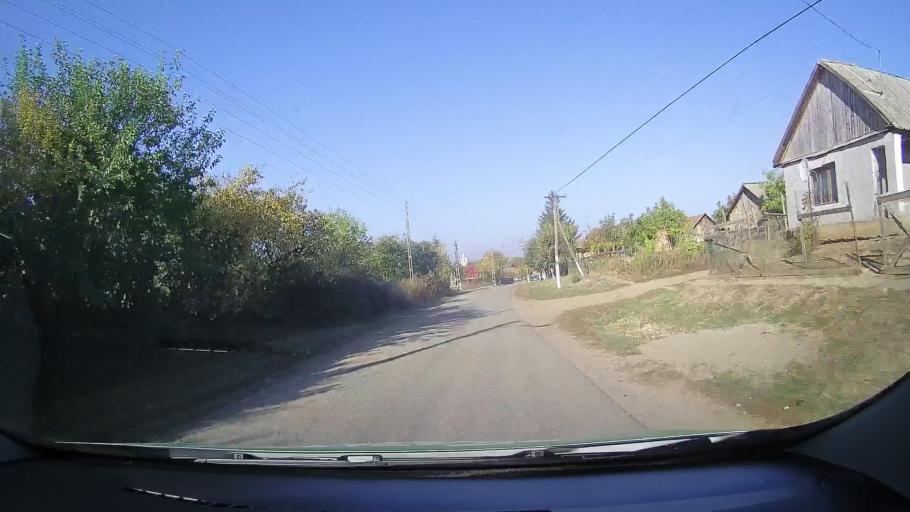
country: RO
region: Satu Mare
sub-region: Comuna Sauca
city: Sauca
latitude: 47.4701
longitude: 22.4933
